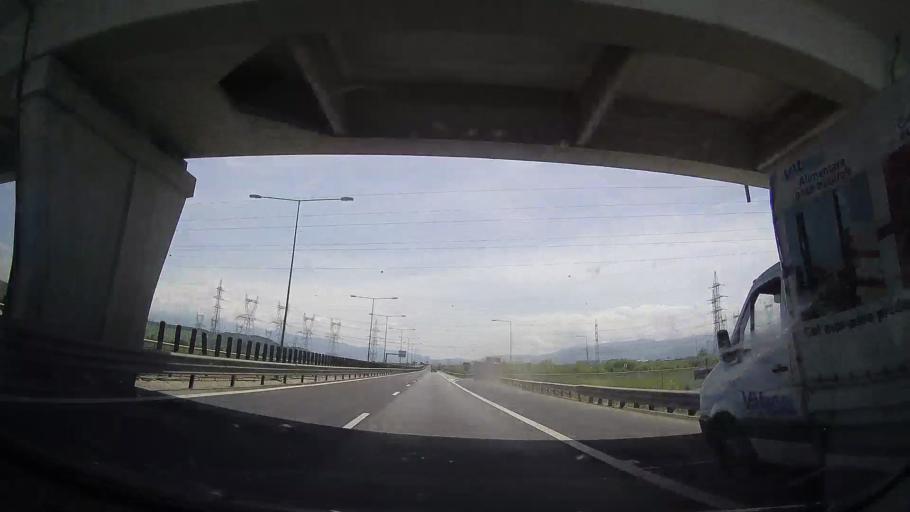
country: RO
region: Sibiu
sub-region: Comuna Selimbar
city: Selimbar
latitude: 45.7892
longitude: 24.1990
